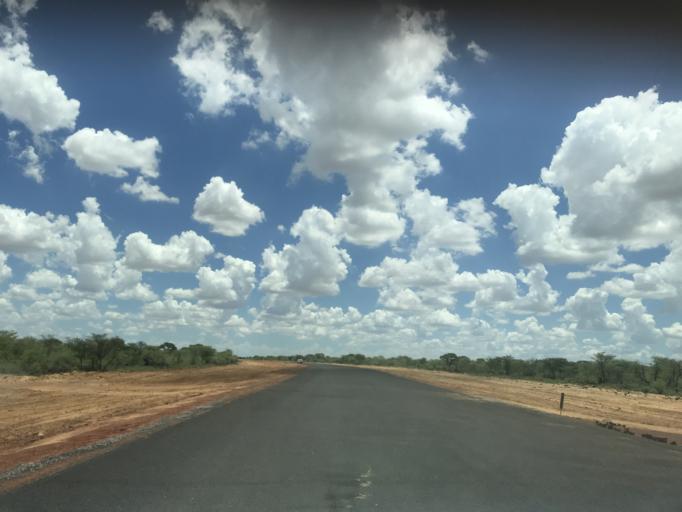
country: BW
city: Mabuli
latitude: -25.8048
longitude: 24.6973
